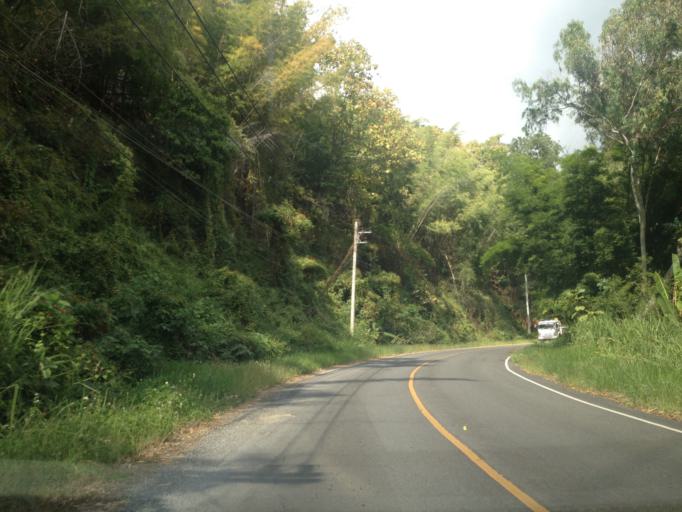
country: TH
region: Chiang Mai
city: Samoeng
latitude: 18.8314
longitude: 98.7819
